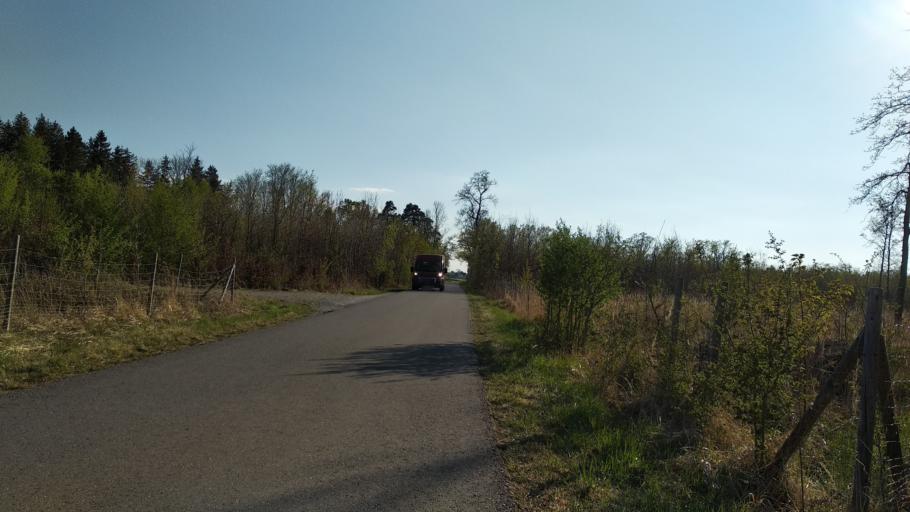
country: DE
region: Bavaria
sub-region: Upper Bavaria
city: Putzbrunn
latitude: 48.0596
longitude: 11.7176
